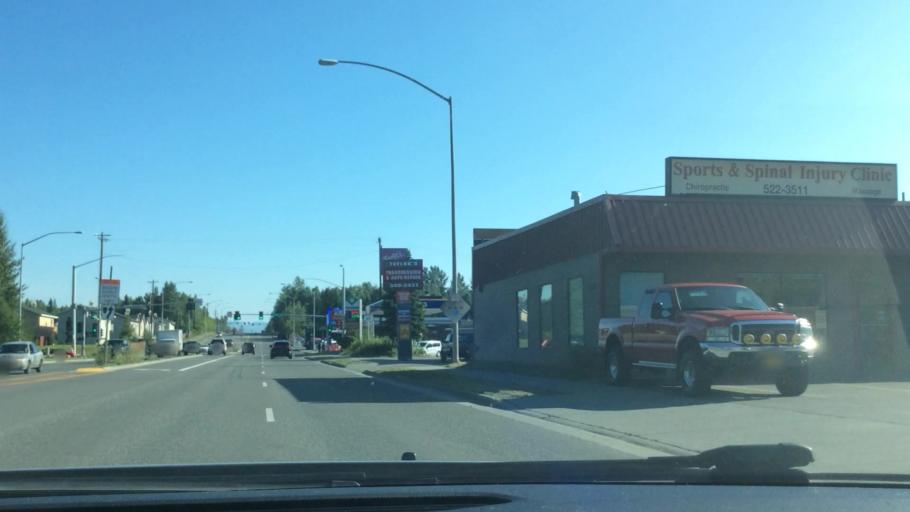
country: US
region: Alaska
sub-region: Anchorage Municipality
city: Anchorage
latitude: 61.1604
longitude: -149.8344
